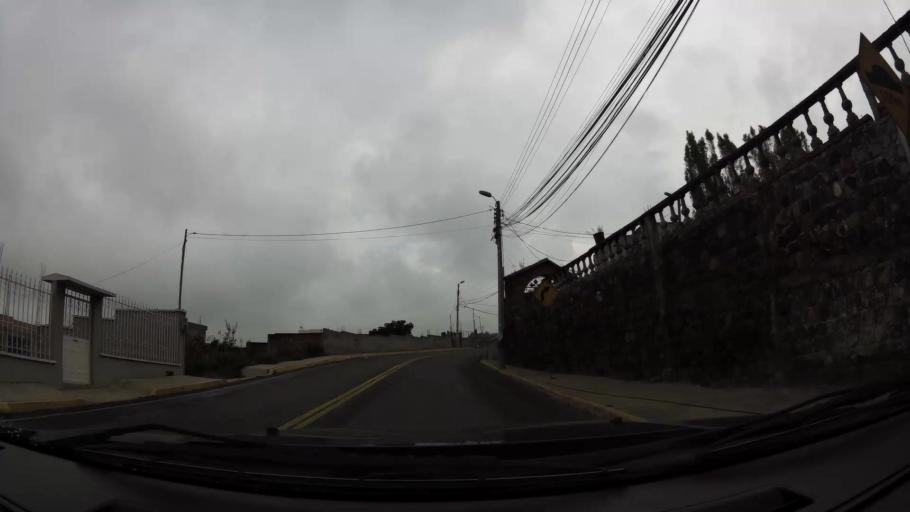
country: EC
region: Pichincha
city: Quito
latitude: -0.2621
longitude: -78.4816
